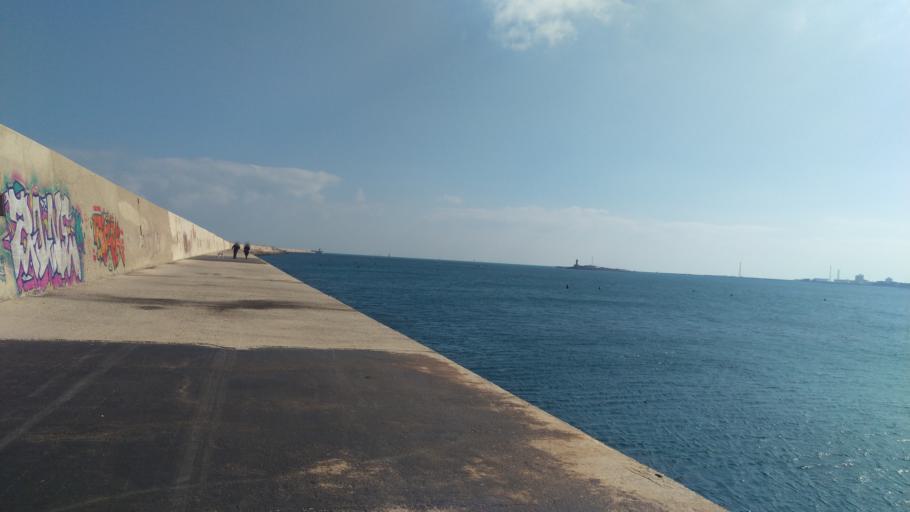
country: IT
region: Apulia
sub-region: Provincia di Brindisi
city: Materdomini
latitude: 40.6626
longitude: 17.9725
